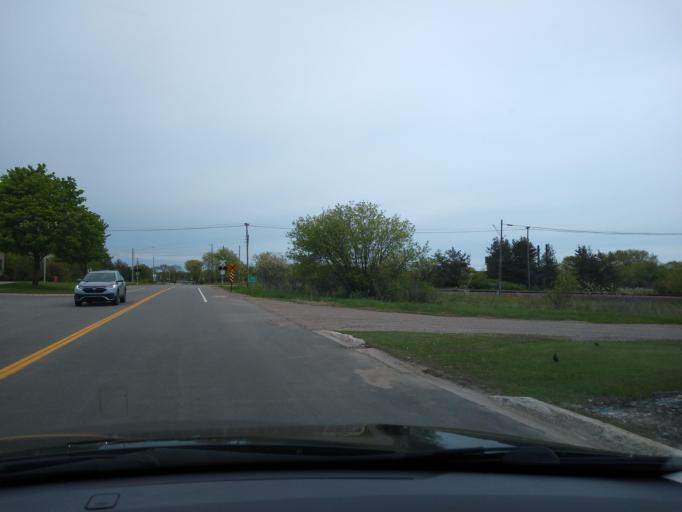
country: US
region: Michigan
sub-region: Delta County
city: Escanaba
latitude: 45.7671
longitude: -87.0691
